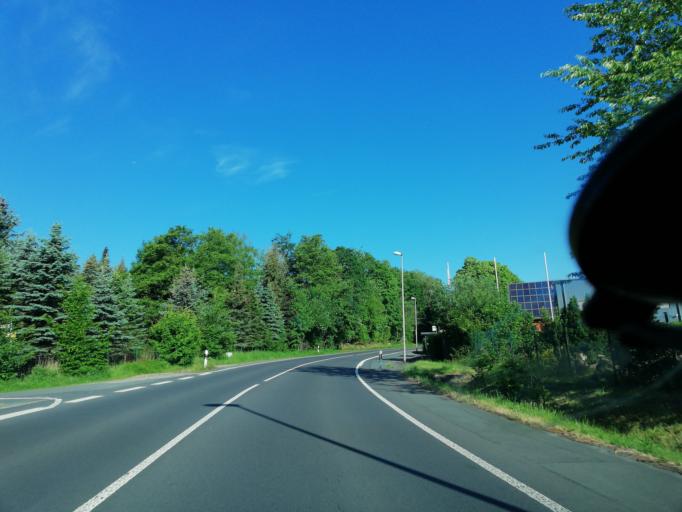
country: DE
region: North Rhine-Westphalia
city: Wetter (Ruhr)
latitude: 51.3926
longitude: 7.3598
